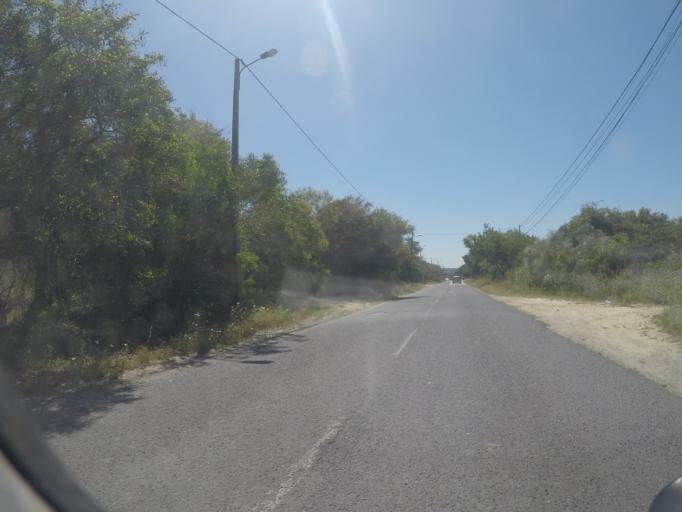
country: PT
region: Setubal
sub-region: Almada
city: Charneca
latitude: 38.6196
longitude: -9.2134
